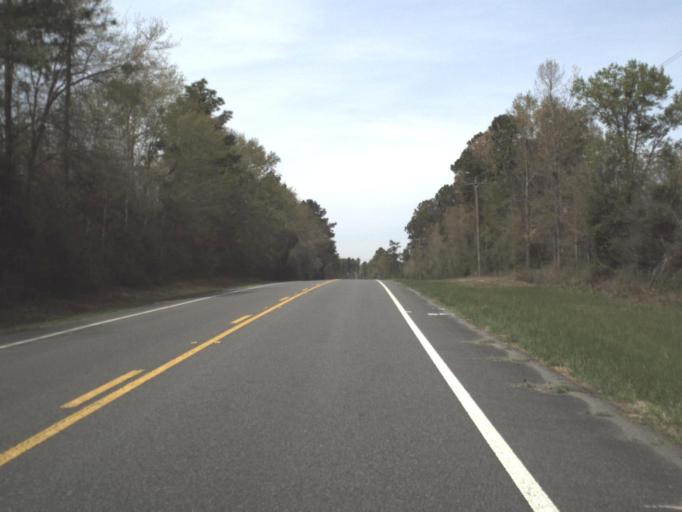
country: US
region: Alabama
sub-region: Geneva County
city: Geneva
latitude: 30.9574
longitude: -85.9902
